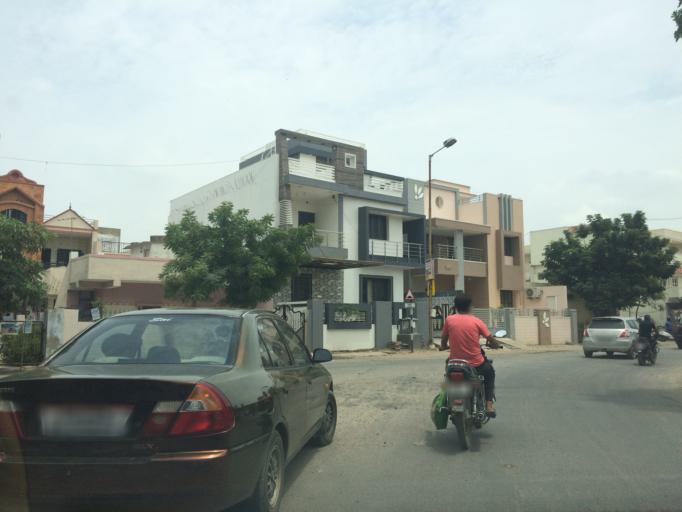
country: IN
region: Gujarat
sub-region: Ahmadabad
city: Ahmedabad
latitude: 23.0813
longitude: 72.5670
